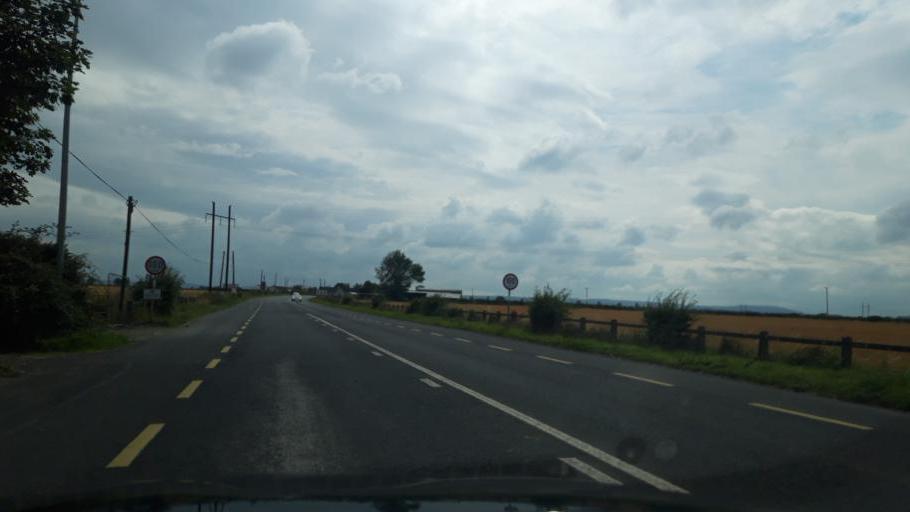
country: IE
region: Leinster
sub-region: Kildare
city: Athy
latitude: 52.9835
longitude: -7.0026
